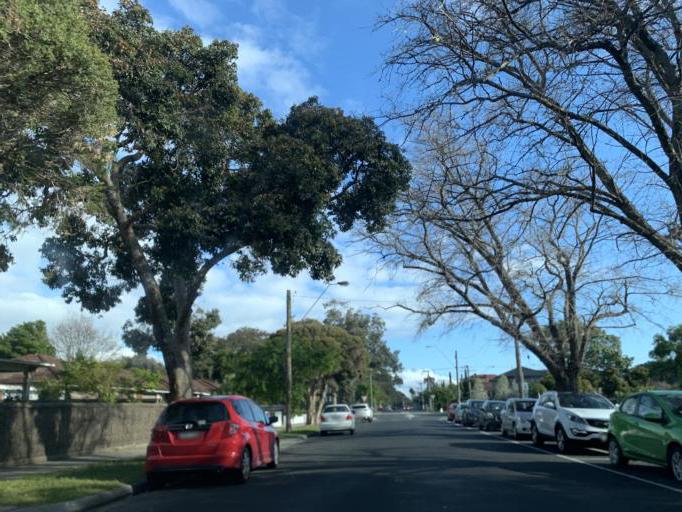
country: AU
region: Victoria
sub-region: Kingston
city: Mentone
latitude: -37.9852
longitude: 145.0648
